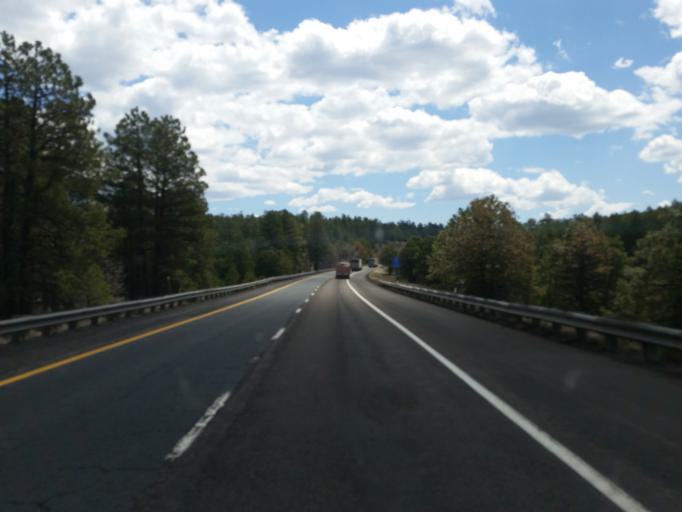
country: US
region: Arizona
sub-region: Coconino County
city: Parks
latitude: 35.2523
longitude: -111.9057
